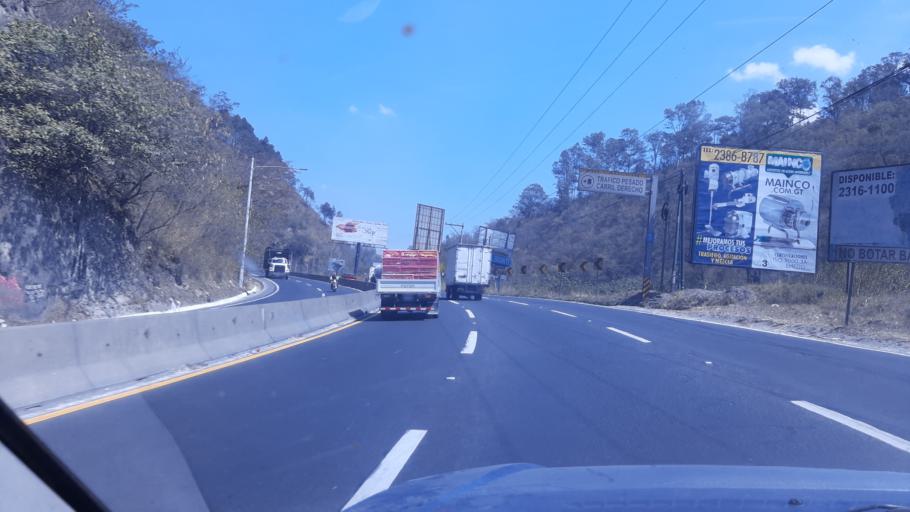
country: GT
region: Guatemala
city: Amatitlan
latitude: 14.4975
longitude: -90.6279
